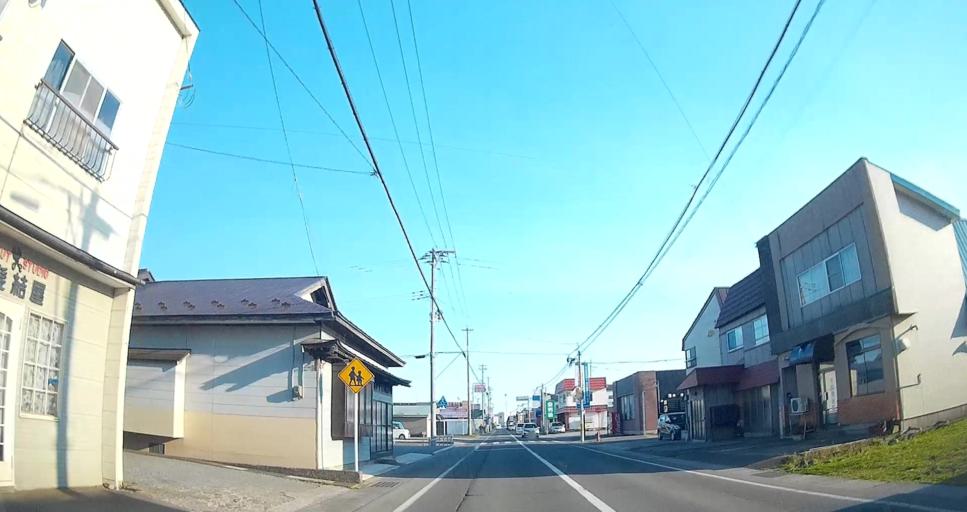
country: JP
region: Aomori
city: Mutsu
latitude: 41.2915
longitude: 141.2108
